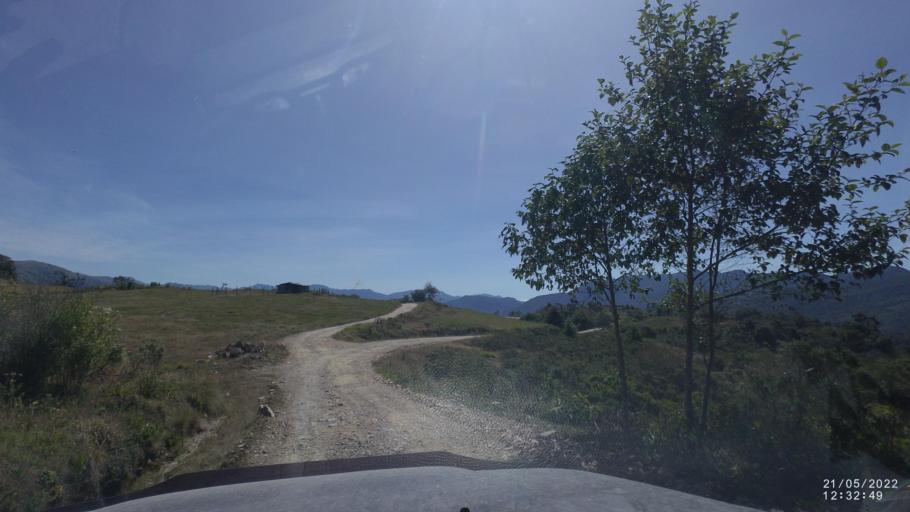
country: BO
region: Cochabamba
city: Colomi
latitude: -17.2053
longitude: -65.9146
